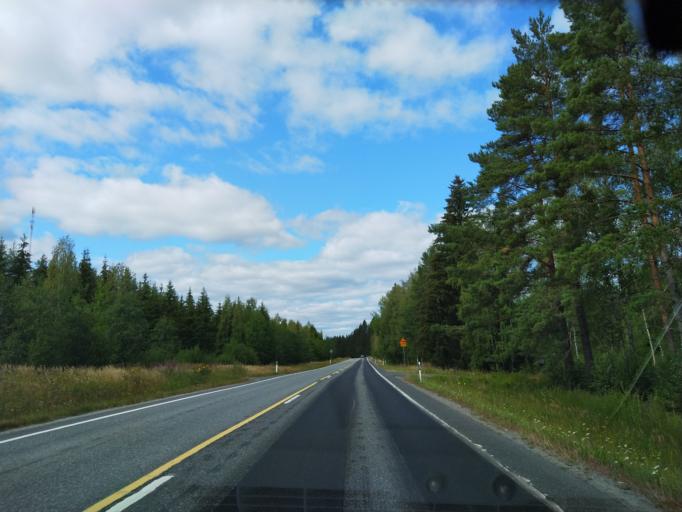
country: FI
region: Haeme
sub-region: Haemeenlinna
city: Tervakoski
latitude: 60.7426
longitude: 24.6720
